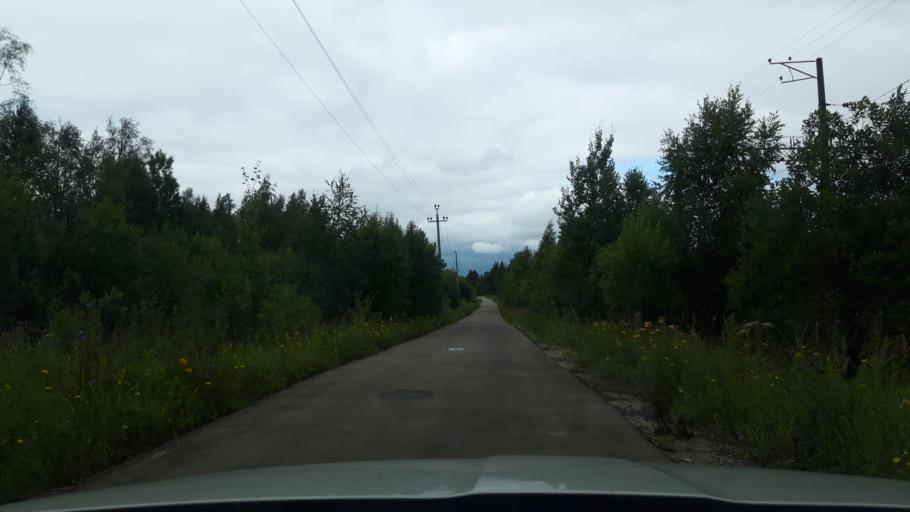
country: RU
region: Moskovskaya
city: Povarovo
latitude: 56.0413
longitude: 37.0542
